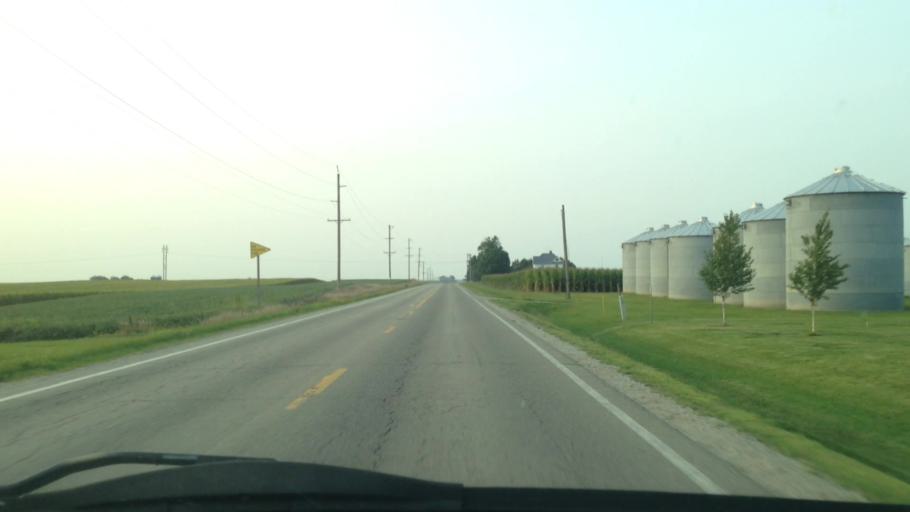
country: US
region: Iowa
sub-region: Iowa County
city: Marengo
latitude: 41.9385
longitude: -92.0849
